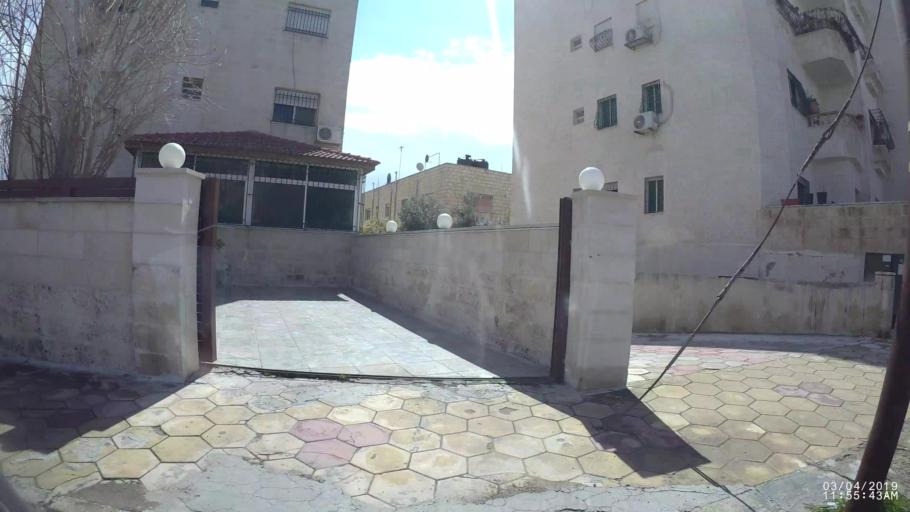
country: JO
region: Amman
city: Wadi as Sir
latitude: 31.9581
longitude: 35.8426
